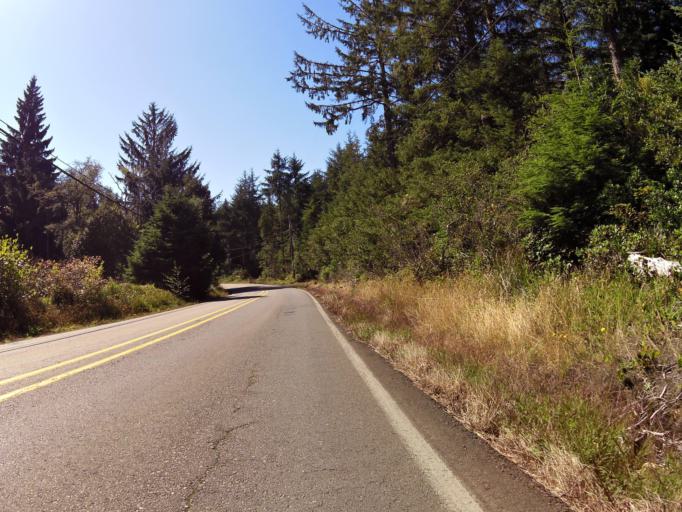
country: US
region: Oregon
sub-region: Coos County
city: Barview
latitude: 43.3295
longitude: -124.3401
